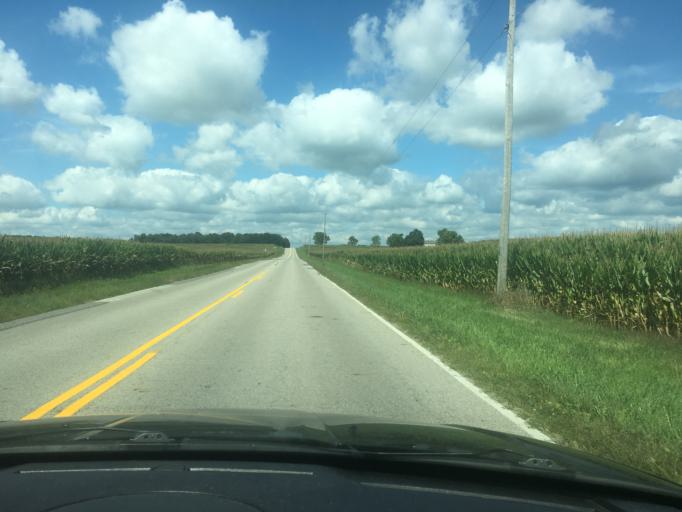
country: US
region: Ohio
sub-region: Logan County
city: West Liberty
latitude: 40.2295
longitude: -83.7080
